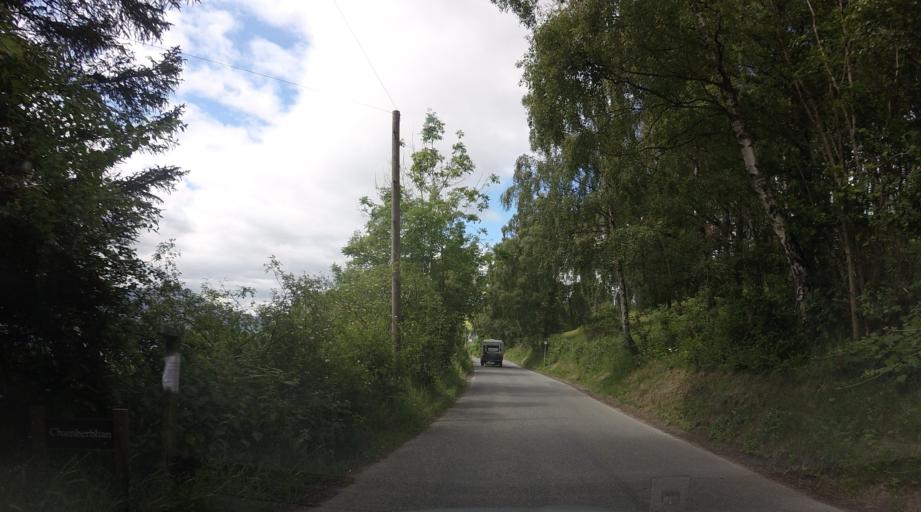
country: GB
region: Scotland
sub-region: Perth and Kinross
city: Aberfeldy
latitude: 56.7181
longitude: -3.9274
